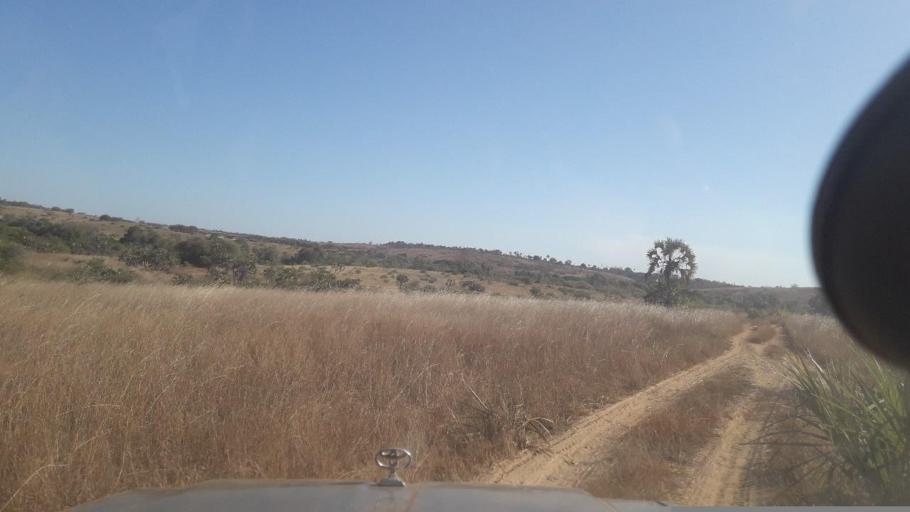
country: MG
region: Boeny
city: Sitampiky
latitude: -16.3749
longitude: 45.5929
